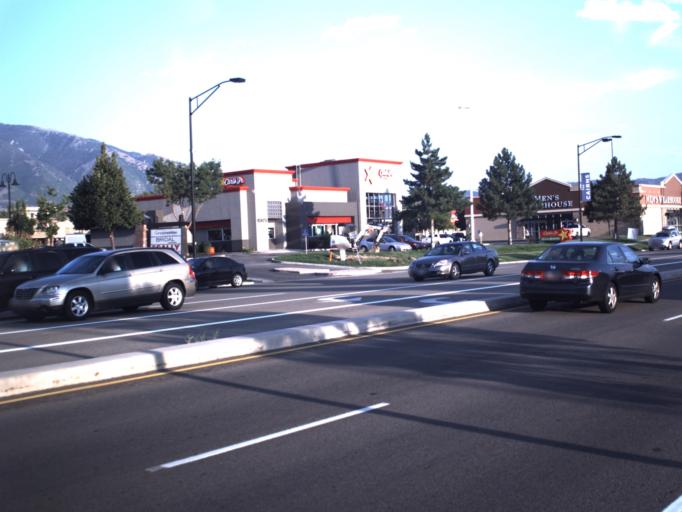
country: US
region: Utah
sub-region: Salt Lake County
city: White City
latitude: 40.5620
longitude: -111.8910
